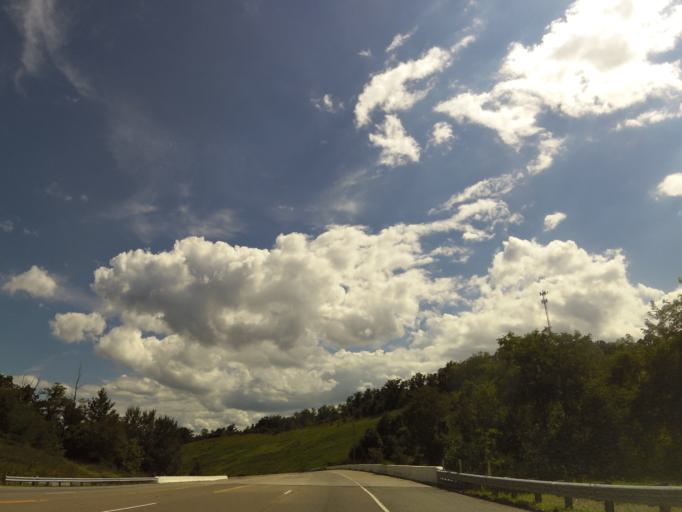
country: US
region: Tennessee
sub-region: Claiborne County
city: Tazewell
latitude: 36.4308
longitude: -83.5574
